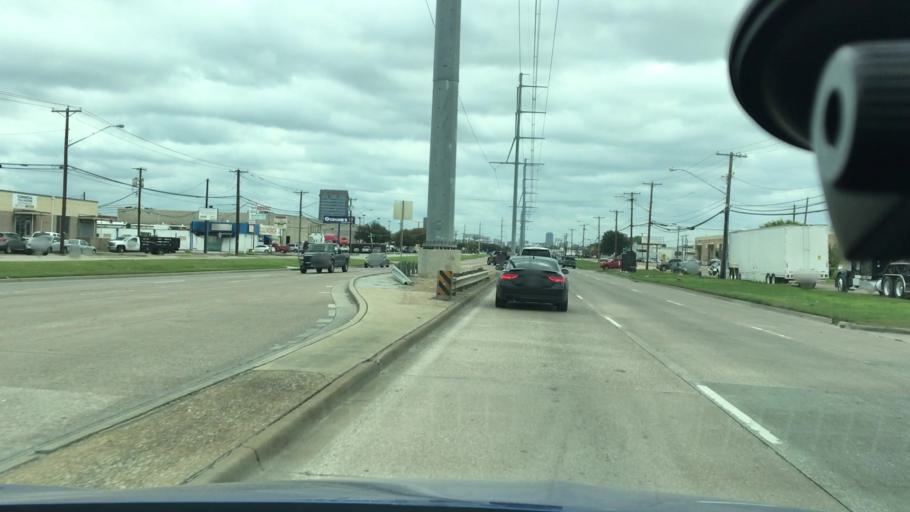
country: US
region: Texas
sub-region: Dallas County
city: Dallas
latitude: 32.8080
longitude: -96.8730
